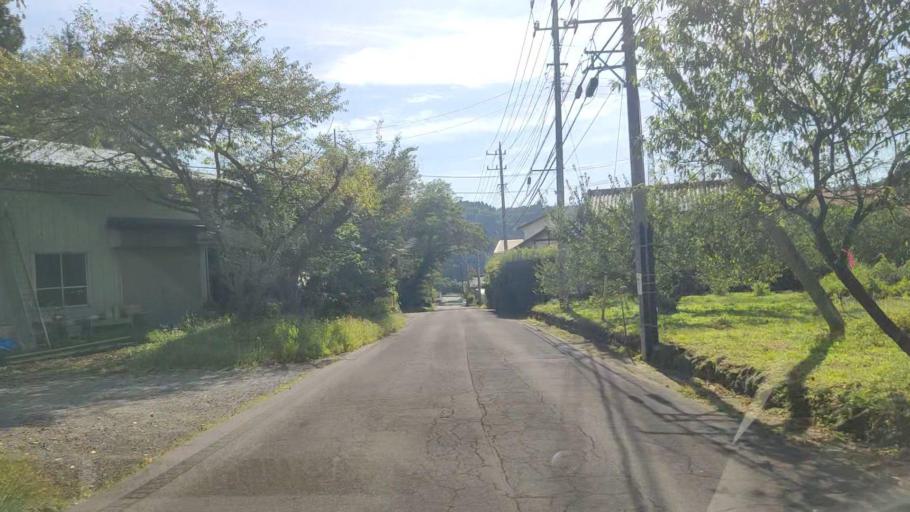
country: JP
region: Gunma
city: Nakanojomachi
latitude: 36.6206
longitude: 138.7775
